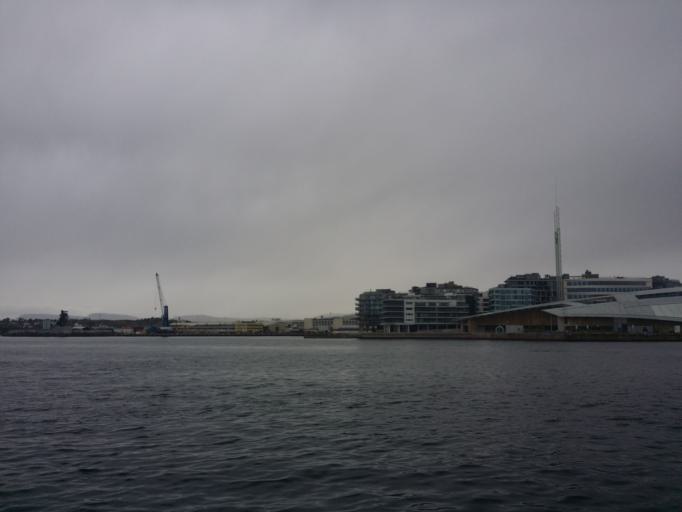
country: NO
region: Oslo
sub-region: Oslo
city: Oslo
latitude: 59.9044
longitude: 10.7244
